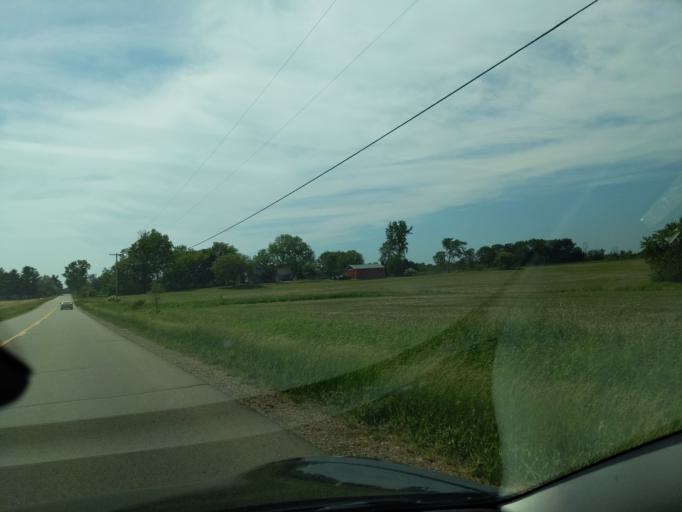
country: US
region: Michigan
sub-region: Eaton County
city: Grand Ledge
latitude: 42.7119
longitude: -84.7700
